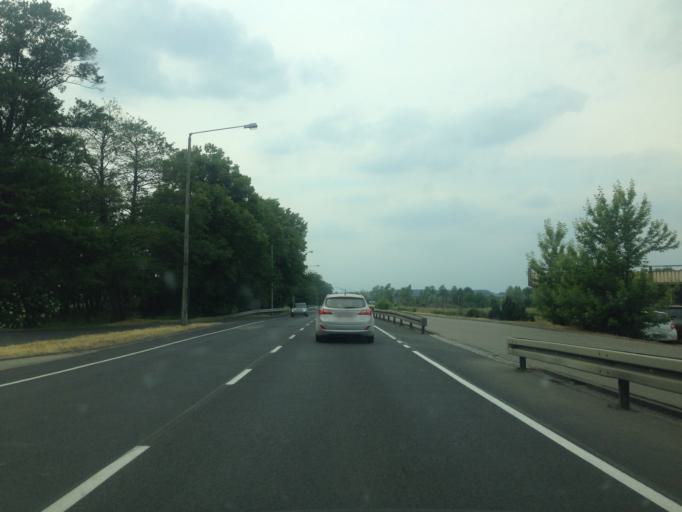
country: PL
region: Kujawsko-Pomorskie
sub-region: Grudziadz
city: Grudziadz
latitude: 53.5048
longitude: 18.8365
